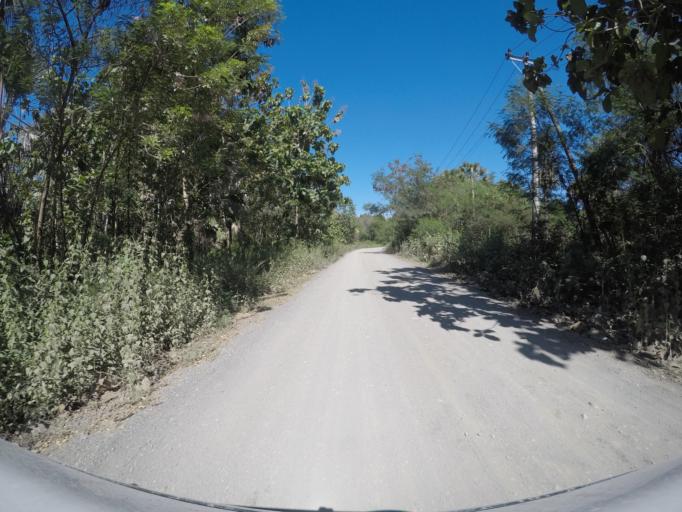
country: TL
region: Viqueque
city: Viqueque
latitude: -8.9743
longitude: 126.0657
